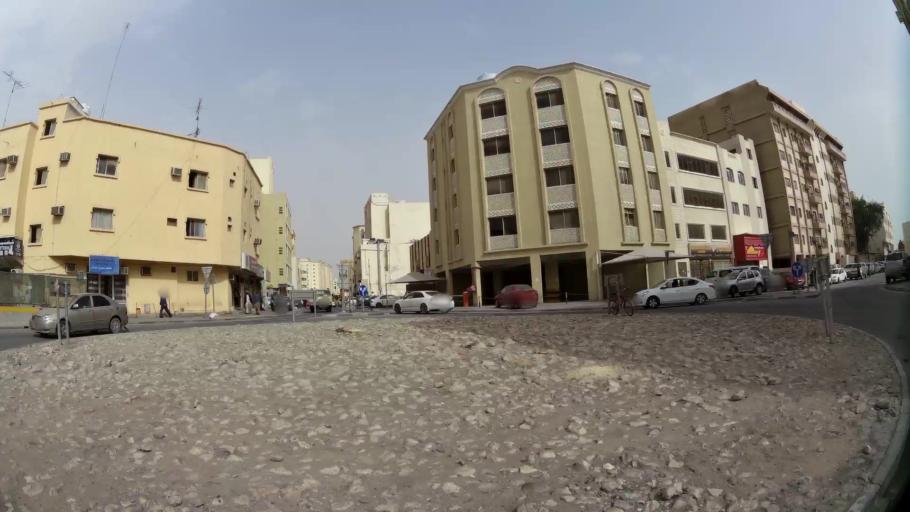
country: QA
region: Baladiyat ad Dawhah
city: Doha
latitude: 25.2745
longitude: 51.5463
